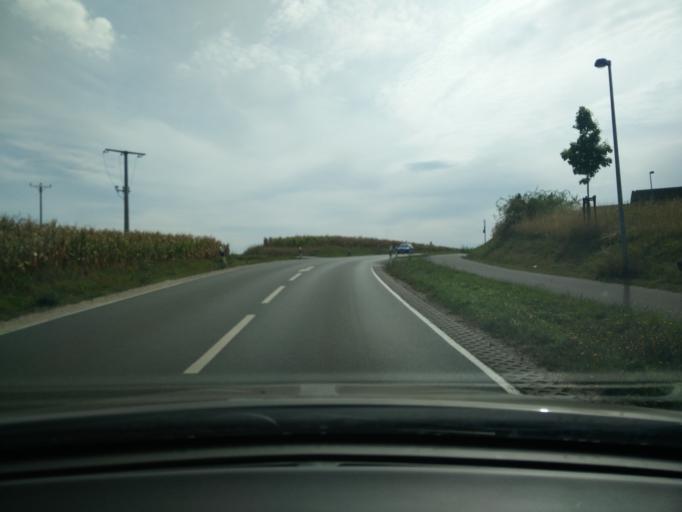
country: DE
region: Bavaria
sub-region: Regierungsbezirk Mittelfranken
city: Veitsbronn
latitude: 49.5043
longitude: 10.8802
